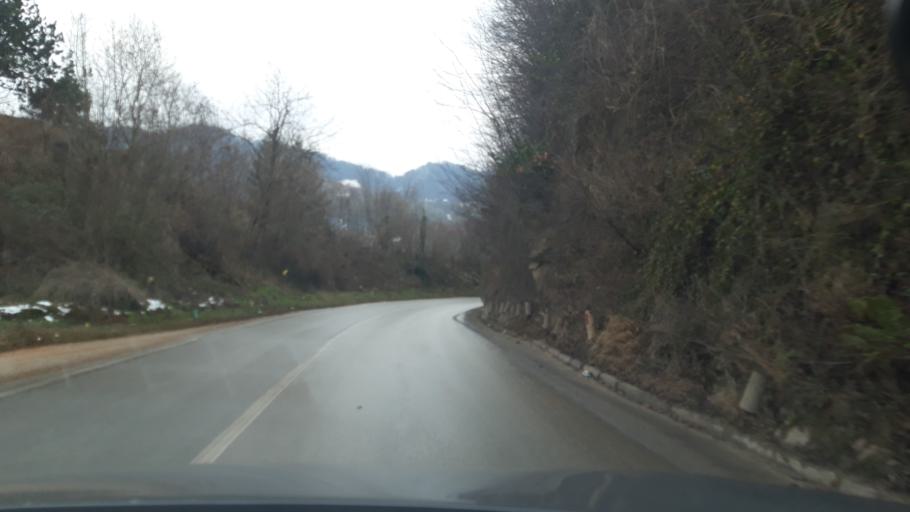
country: RS
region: Central Serbia
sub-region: Macvanski Okrug
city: Mali Zvornik
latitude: 44.3531
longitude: 19.1069
